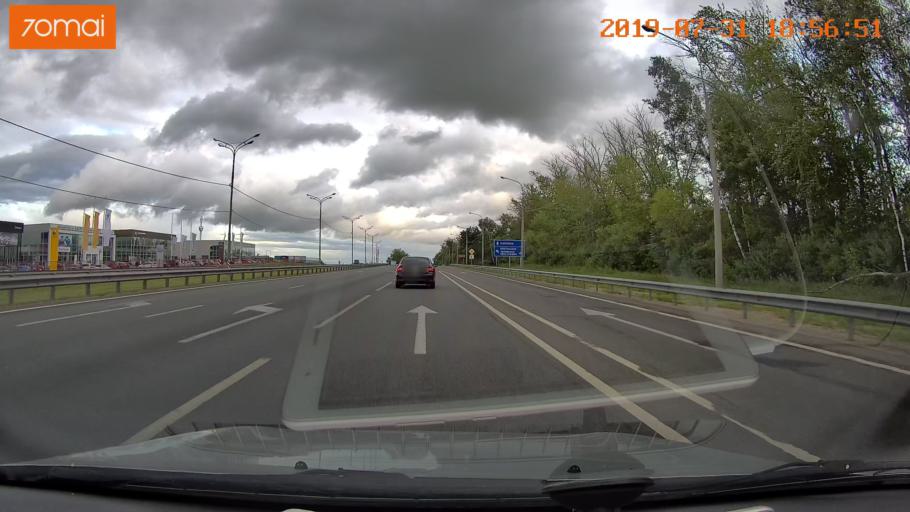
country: RU
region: Moskovskaya
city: Raduzhnyy
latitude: 55.1592
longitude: 38.6839
